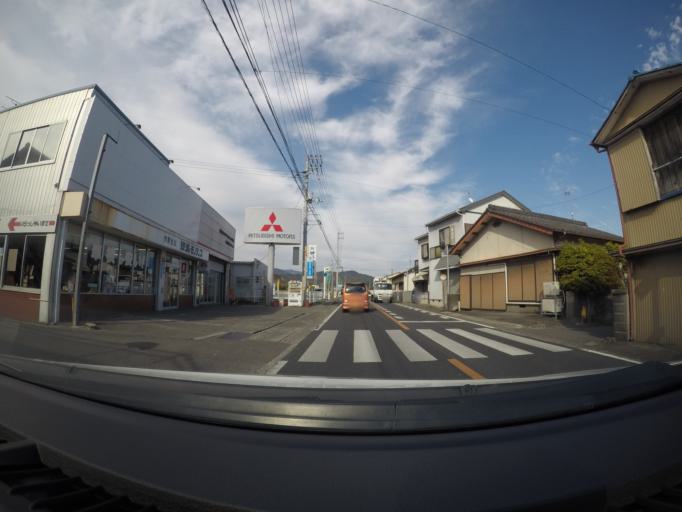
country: JP
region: Kochi
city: Kochi-shi
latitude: 33.6120
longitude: 133.7096
